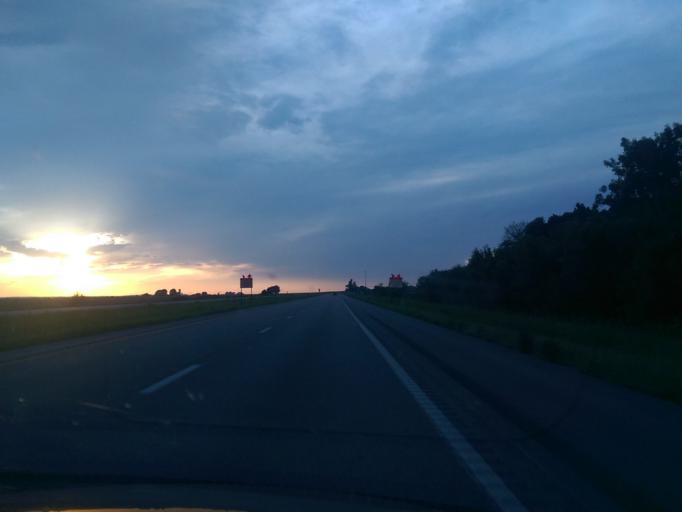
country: US
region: Missouri
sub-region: Atchison County
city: Rock Port
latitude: 40.3454
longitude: -95.5065
